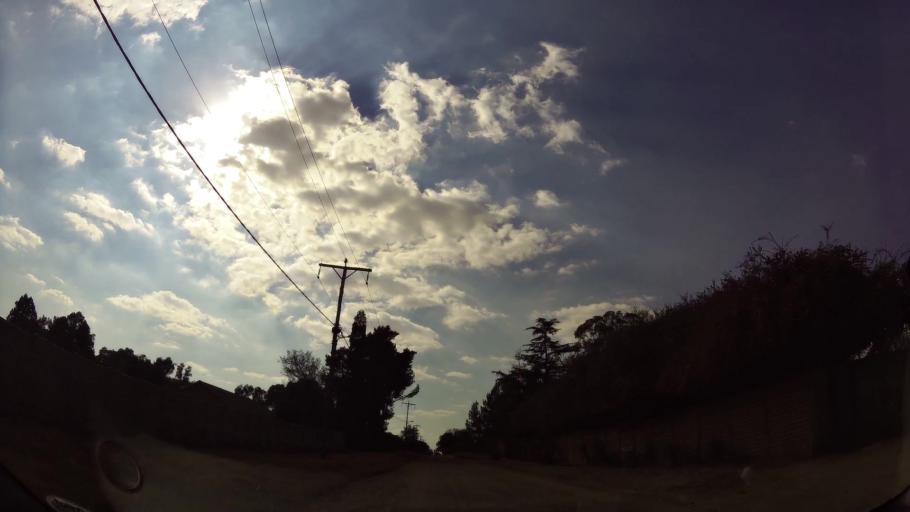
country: ZA
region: Gauteng
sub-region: Ekurhuleni Metropolitan Municipality
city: Benoni
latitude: -26.0931
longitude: 28.3557
